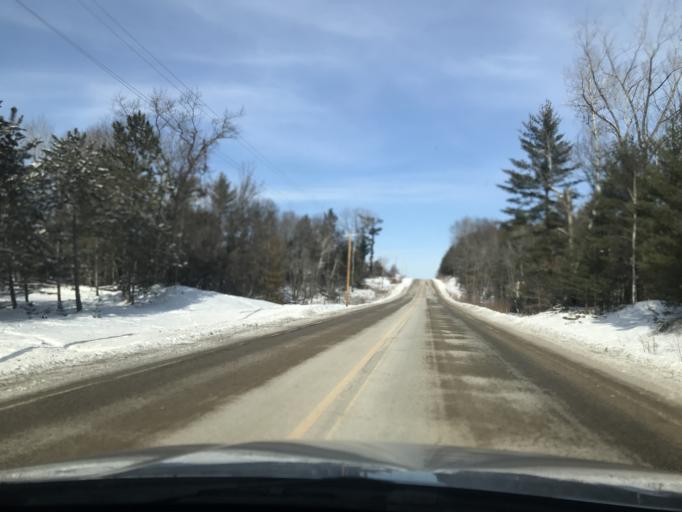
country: US
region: Wisconsin
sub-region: Oconto County
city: Oconto Falls
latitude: 45.1406
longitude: -88.1772
